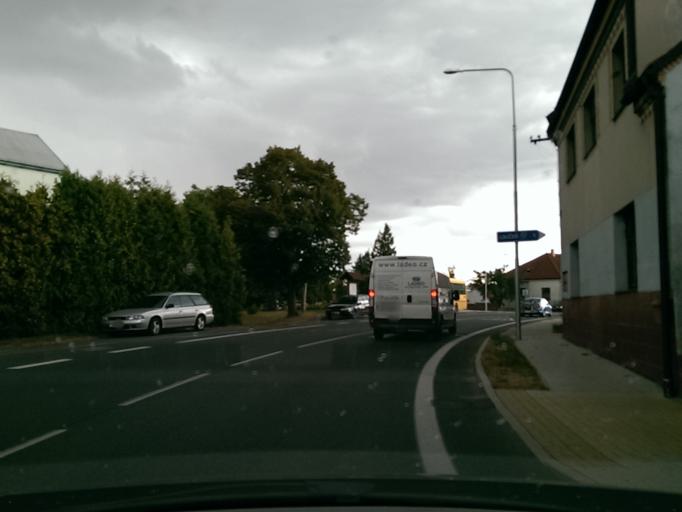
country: CZ
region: Central Bohemia
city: Lustenice
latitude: 50.2709
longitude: 14.9615
